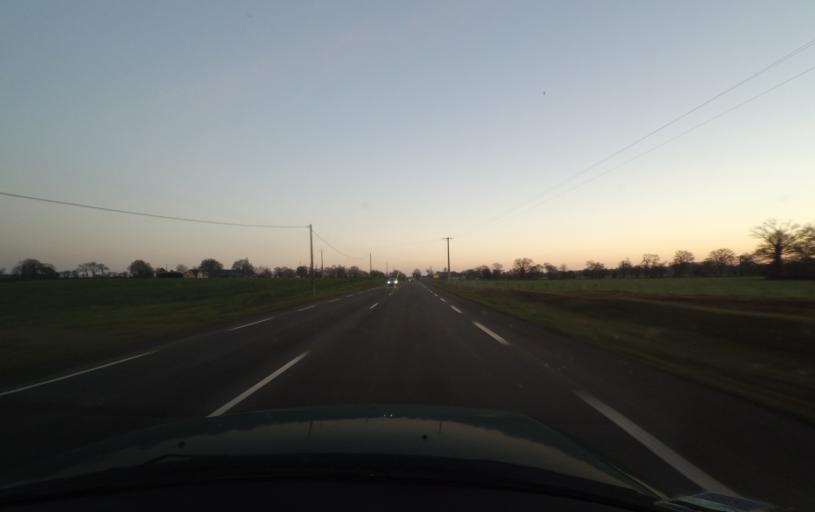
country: FR
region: Pays de la Loire
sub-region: Departement de la Mayenne
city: Soulge-sur-Ouette
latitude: 48.0842
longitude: -0.5388
